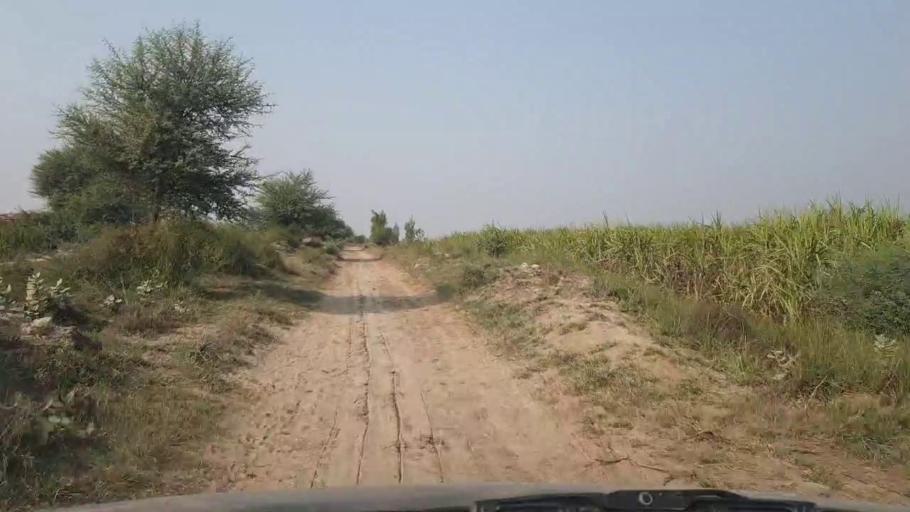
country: PK
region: Sindh
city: Tando Muhammad Khan
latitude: 25.0661
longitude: 68.3591
